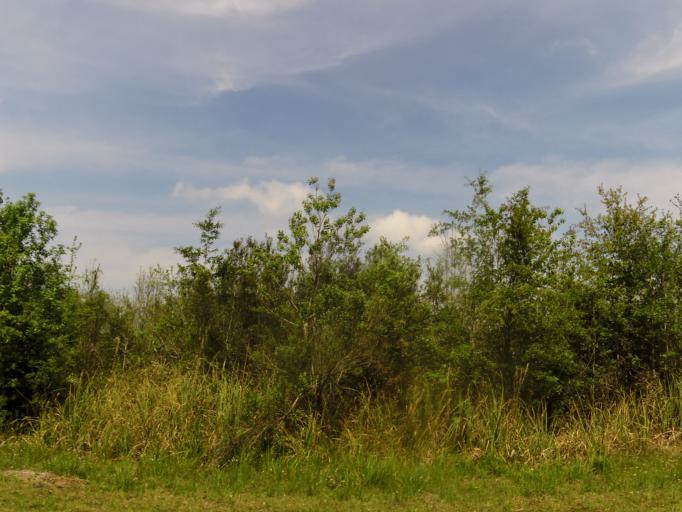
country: US
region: Georgia
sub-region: Camden County
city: Kingsland
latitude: 30.7881
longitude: -81.7133
